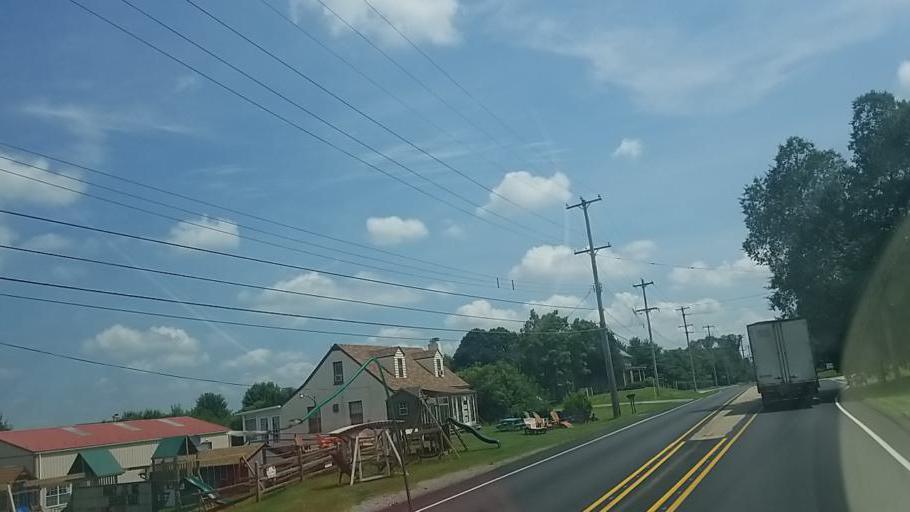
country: US
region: Pennsylvania
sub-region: Chester County
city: Toughkenamon
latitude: 39.8061
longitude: -75.7460
